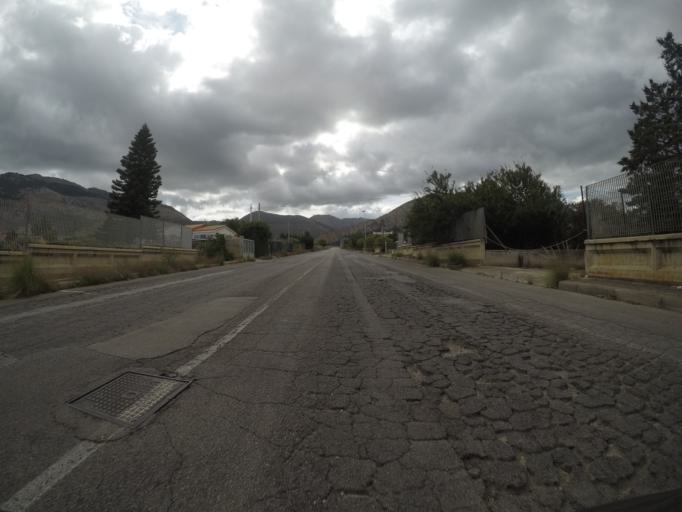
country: IT
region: Sicily
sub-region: Palermo
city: Capaci
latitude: 38.1711
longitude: 13.2201
